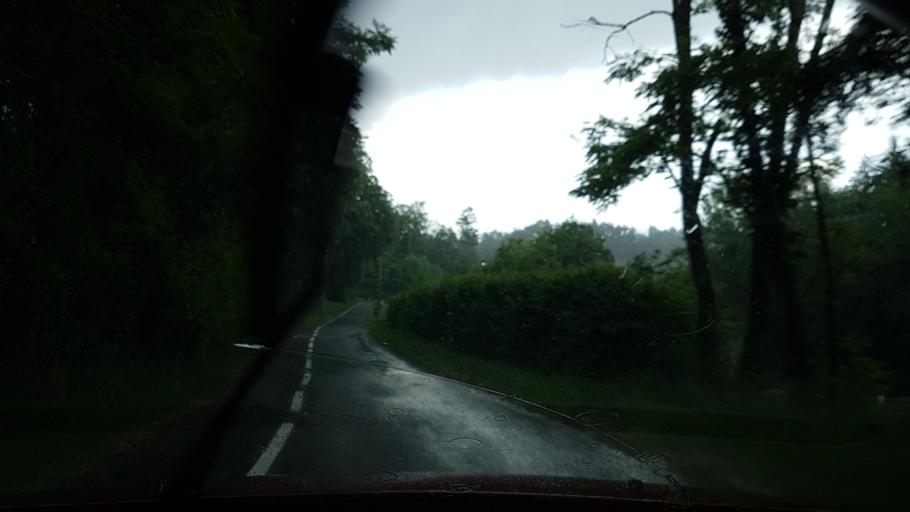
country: FR
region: Franche-Comte
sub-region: Departement du Jura
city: Clairvaux-les-Lacs
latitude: 46.5799
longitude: 5.6976
